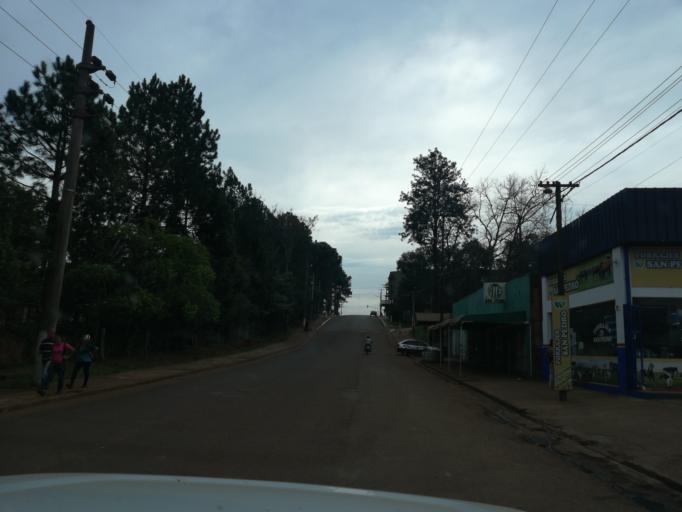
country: AR
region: Misiones
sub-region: Departamento de San Pedro
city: San Pedro
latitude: -26.6268
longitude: -54.1131
